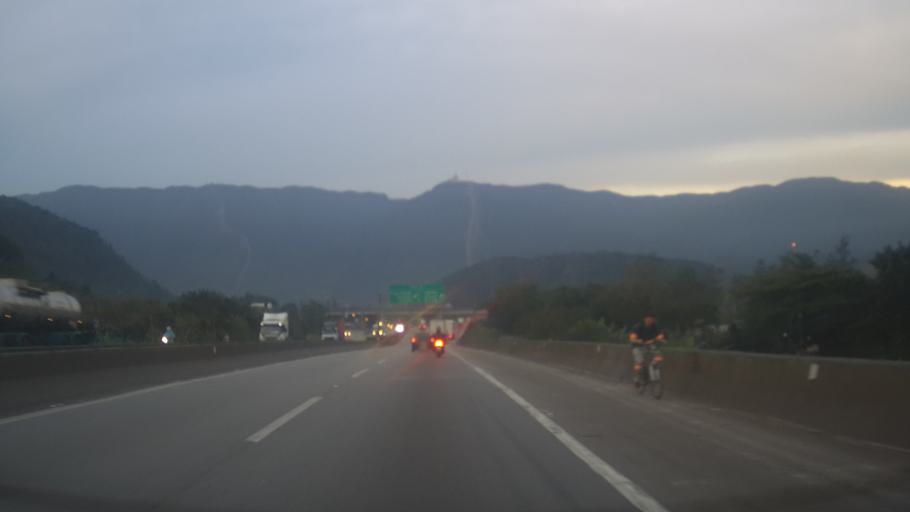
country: BR
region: Sao Paulo
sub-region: Cubatao
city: Cubatao
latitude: -23.8960
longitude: -46.4328
